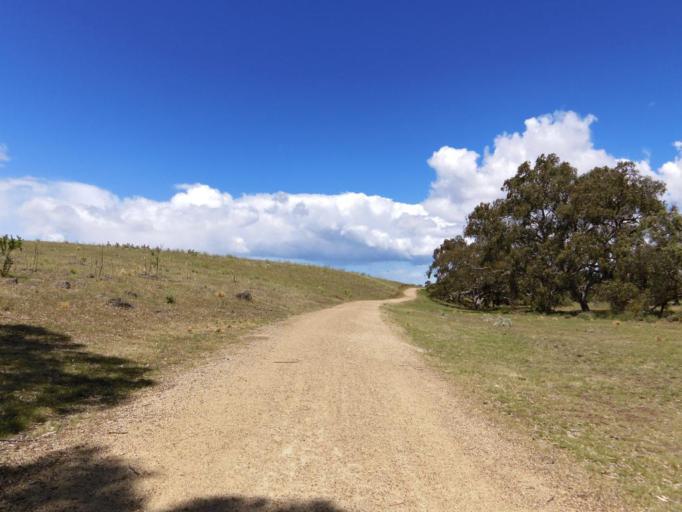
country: AU
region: Victoria
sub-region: Hume
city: Greenvale
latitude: -37.6522
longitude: 144.8471
